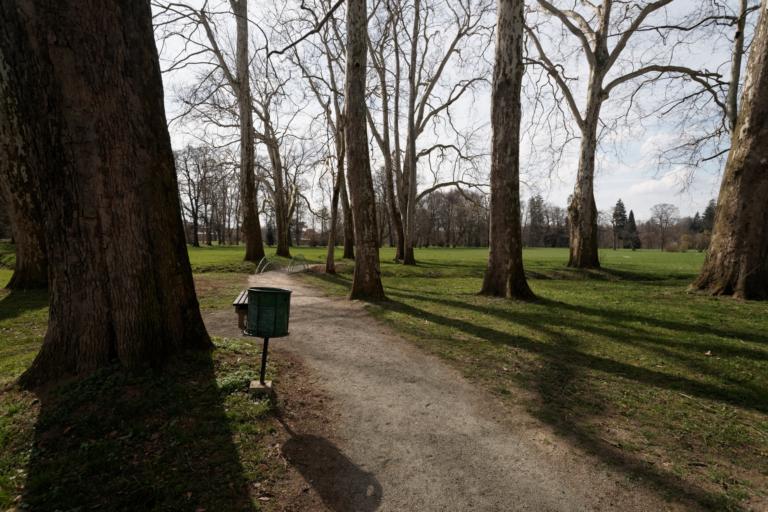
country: CZ
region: Zlin
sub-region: Okres Kromeriz
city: Kromeriz
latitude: 49.3039
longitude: 17.3946
